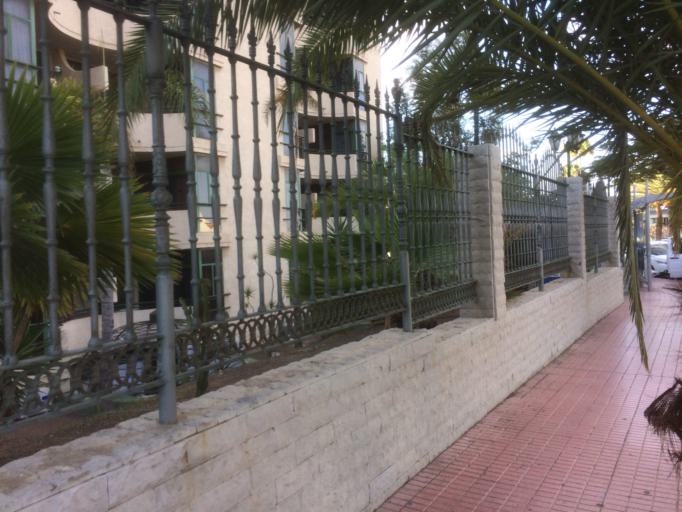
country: ES
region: Canary Islands
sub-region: Provincia de Santa Cruz de Tenerife
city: Playa de las Americas
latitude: 28.0898
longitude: -16.7350
